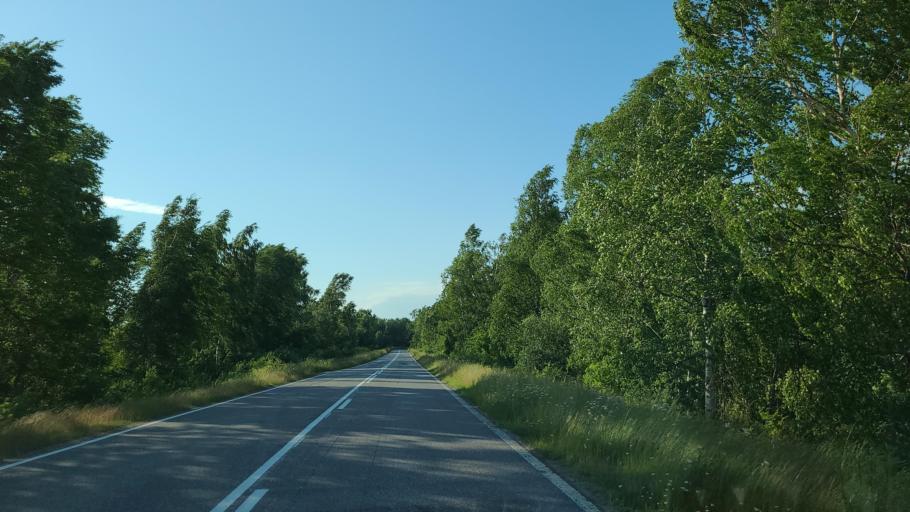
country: FI
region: Ostrobothnia
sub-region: Vaasa
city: Replot
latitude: 63.2826
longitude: 21.3362
